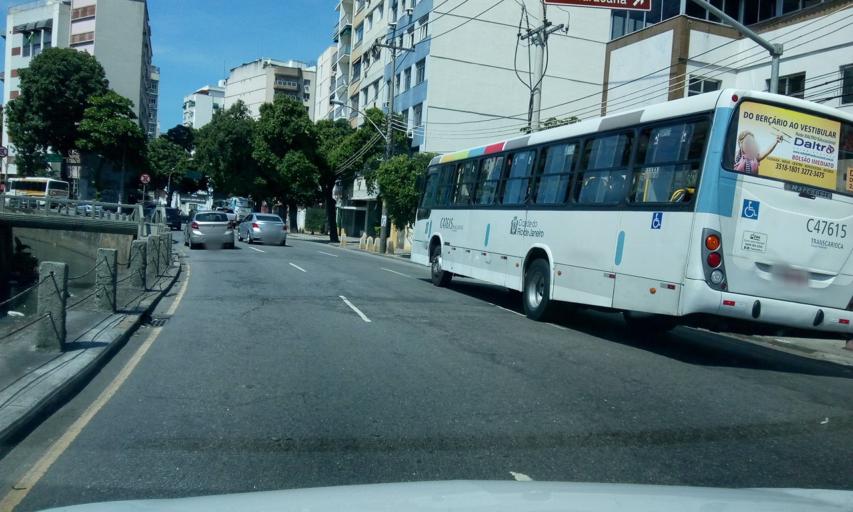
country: BR
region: Rio de Janeiro
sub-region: Rio De Janeiro
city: Rio de Janeiro
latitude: -22.9154
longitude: -43.2346
